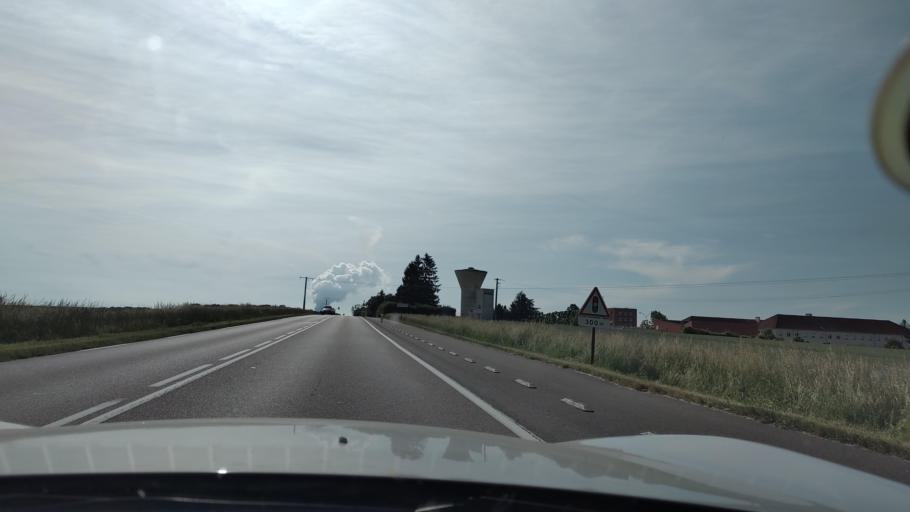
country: FR
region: Ile-de-France
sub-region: Departement de Seine-et-Marne
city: Sourdun
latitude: 48.5344
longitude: 3.3676
